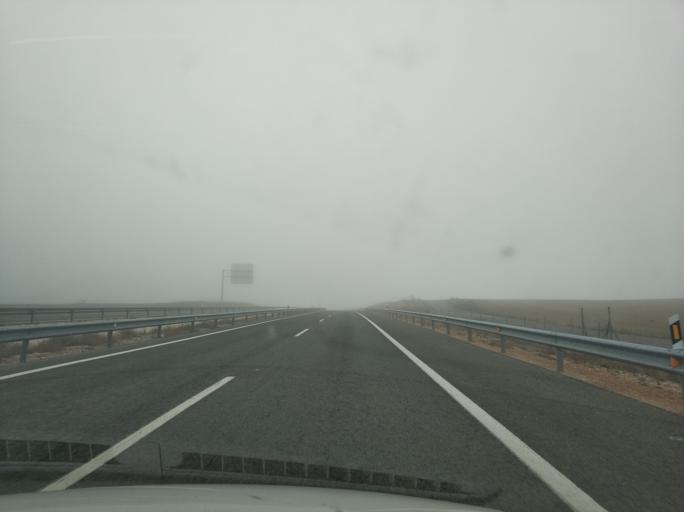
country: ES
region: Castille and Leon
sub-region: Provincia de Soria
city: Adradas
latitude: 41.3396
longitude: -2.4817
